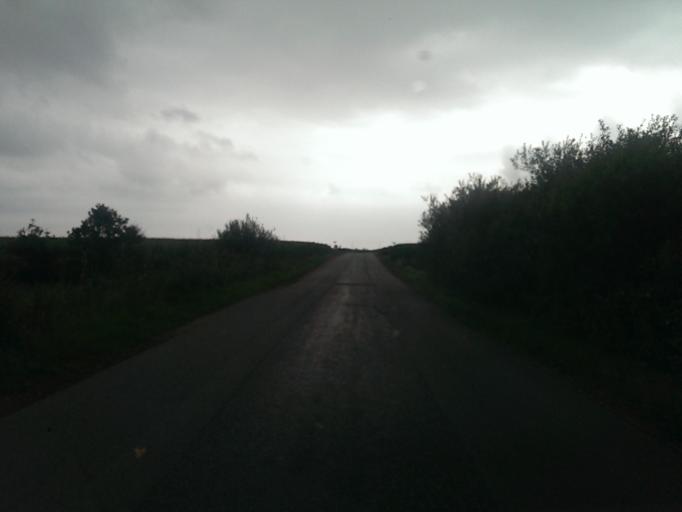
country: DK
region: South Denmark
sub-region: Esbjerg Kommune
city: Tjaereborg
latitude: 55.5087
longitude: 8.5760
